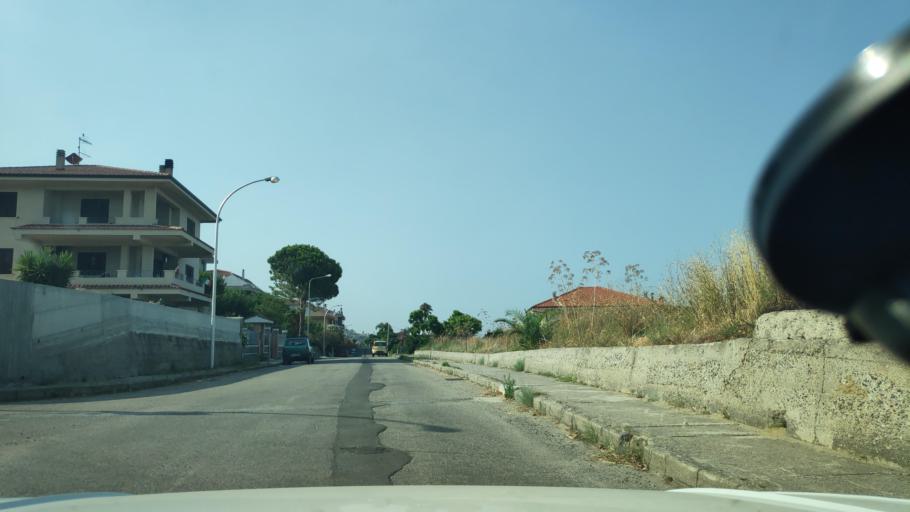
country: IT
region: Calabria
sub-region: Provincia di Catanzaro
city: Santa Caterina dello Ionio Marina
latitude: 38.5314
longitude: 16.5679
